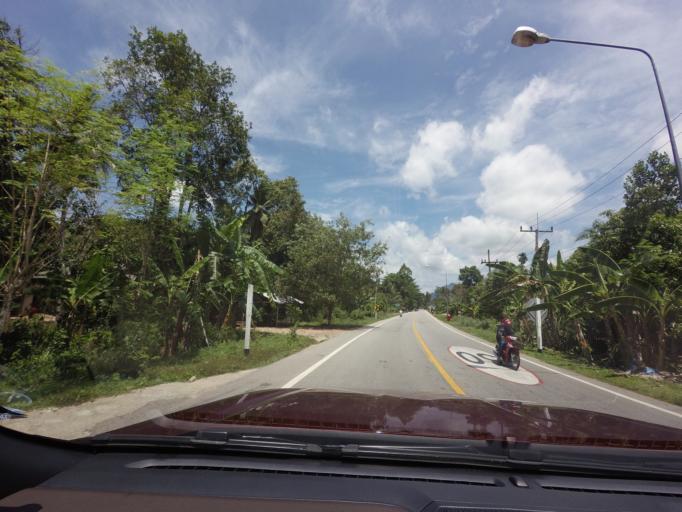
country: TH
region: Narathiwat
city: Ra-ngae
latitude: 6.2610
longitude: 101.6922
